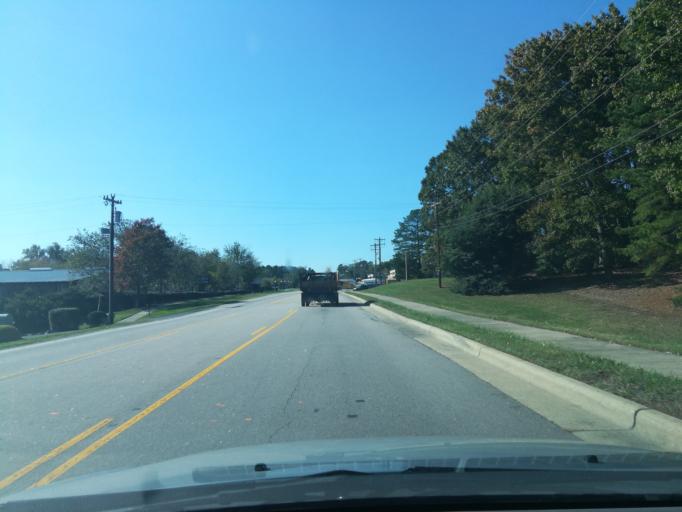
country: US
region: North Carolina
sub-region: Durham County
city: Durham
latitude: 36.0336
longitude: -78.9715
